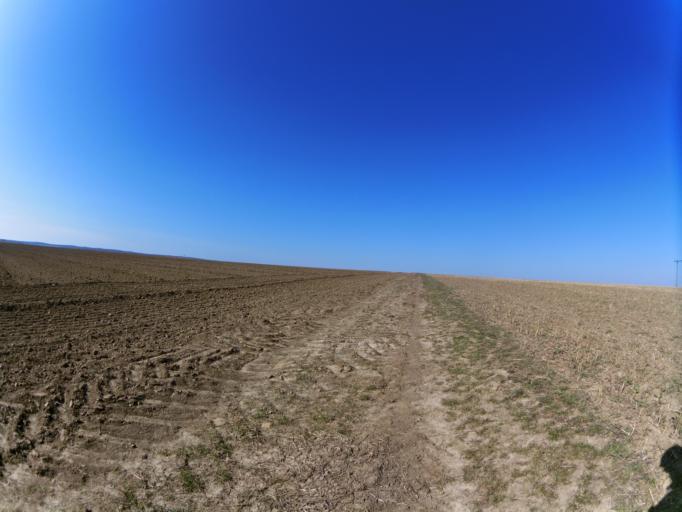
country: DE
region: Bavaria
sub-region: Regierungsbezirk Unterfranken
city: Oberpleichfeld
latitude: 49.8786
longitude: 10.0775
